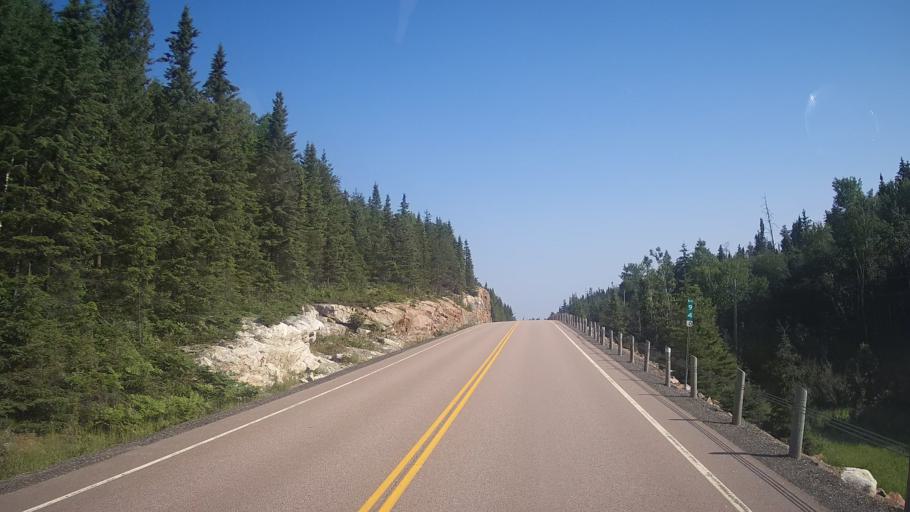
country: CA
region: Ontario
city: Rayside-Balfour
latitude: 46.9988
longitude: -81.6324
